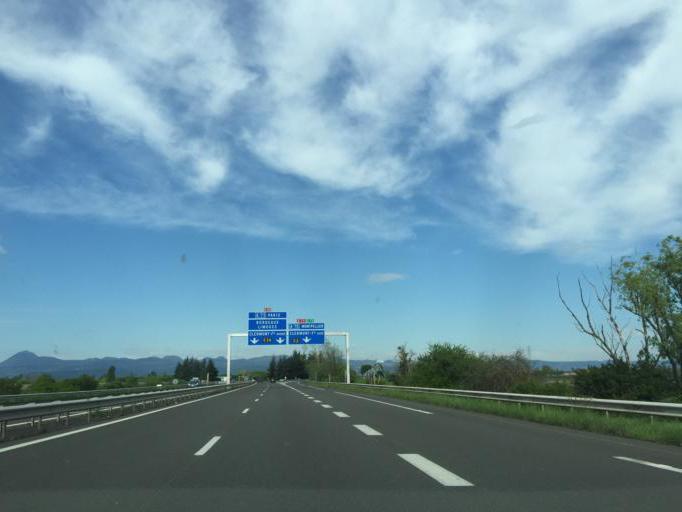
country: FR
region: Auvergne
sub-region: Departement du Puy-de-Dome
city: Pont-du-Chateau
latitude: 45.8290
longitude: 3.2354
